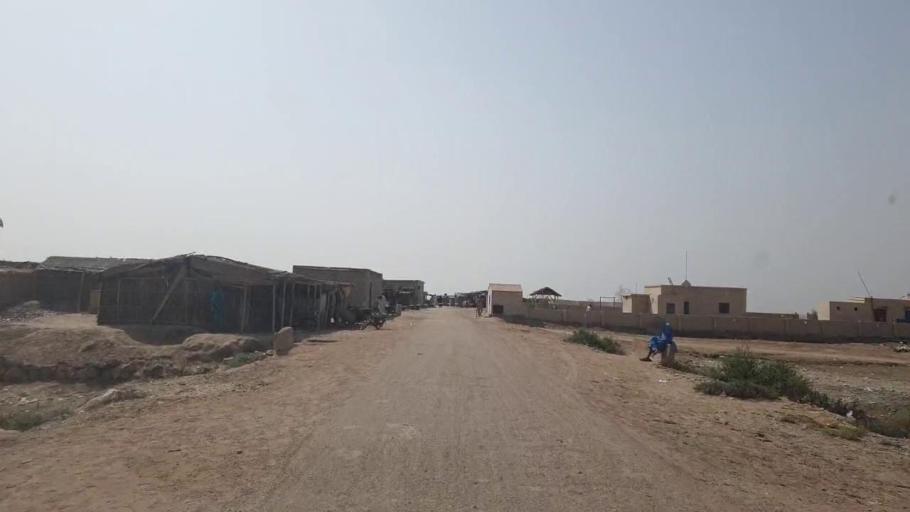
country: PK
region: Sindh
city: Jati
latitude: 24.3368
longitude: 68.5931
